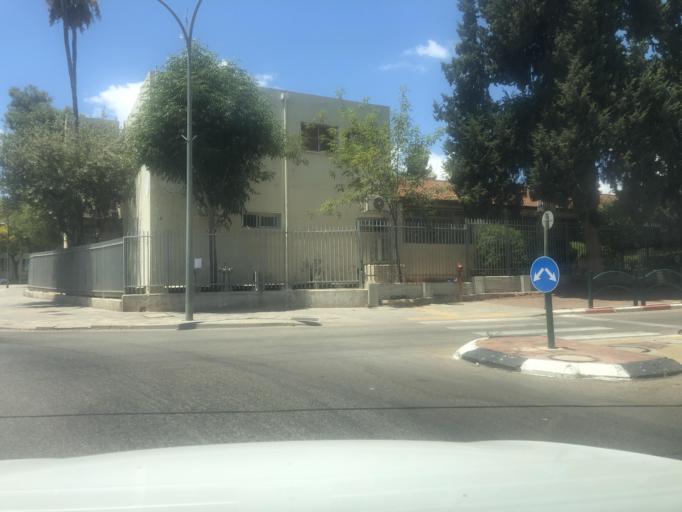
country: IL
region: Central District
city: Hod HaSharon
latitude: 32.1602
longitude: 34.9045
